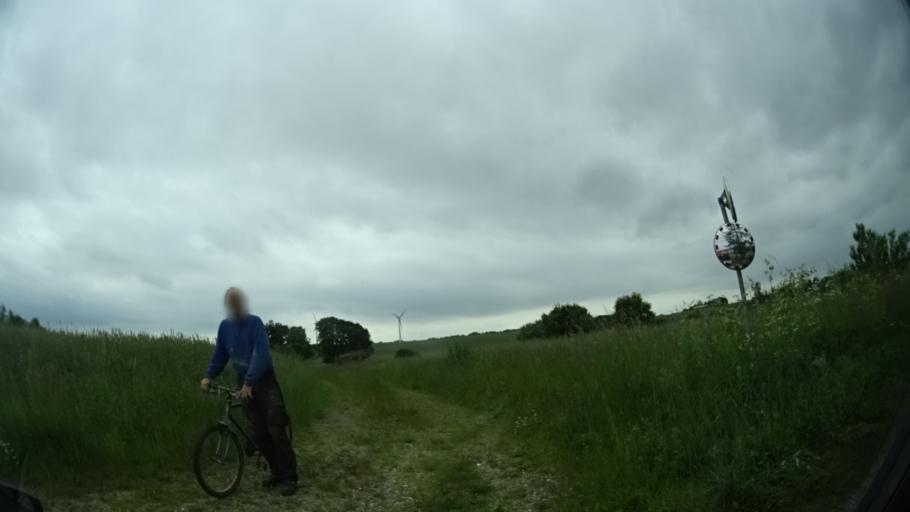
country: DK
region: Central Jutland
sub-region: Arhus Kommune
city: Solbjerg
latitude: 56.0755
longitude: 10.0889
